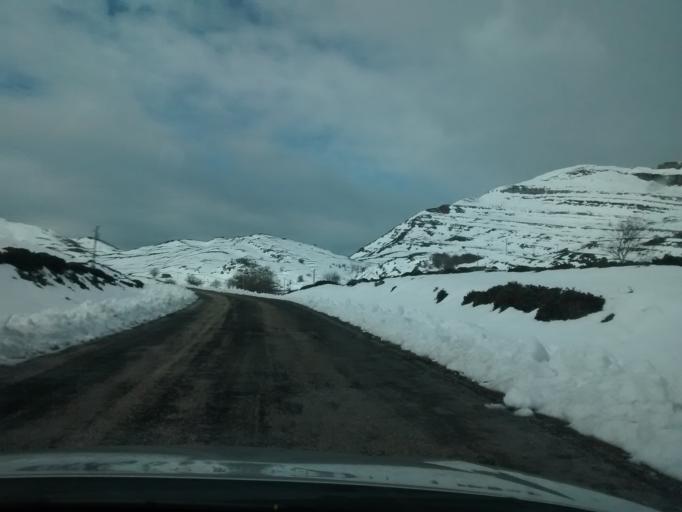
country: ES
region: Cantabria
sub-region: Provincia de Cantabria
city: Arredondo
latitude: 43.1650
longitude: -3.6381
